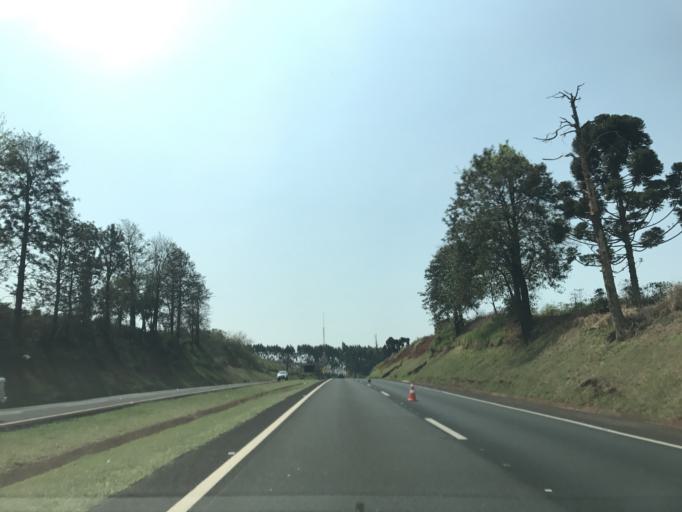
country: BR
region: Parana
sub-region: Rolandia
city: Rolandia
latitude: -23.3075
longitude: -51.3303
